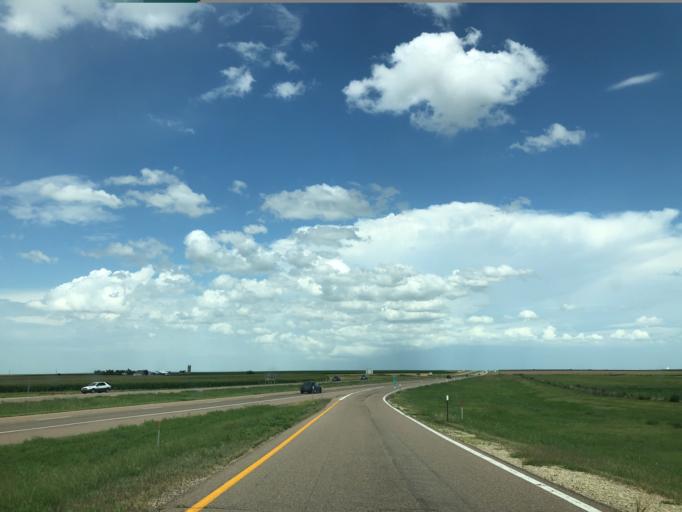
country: US
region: Kansas
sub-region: Gove County
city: Gove
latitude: 39.0968
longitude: -100.3690
